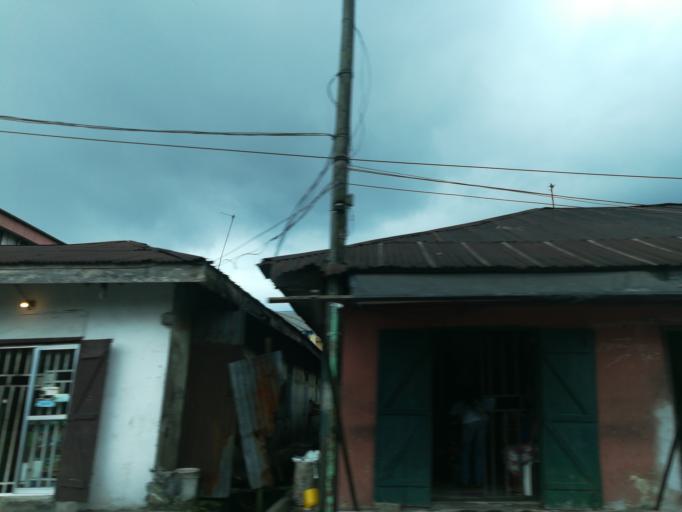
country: NG
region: Rivers
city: Port Harcourt
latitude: 4.7964
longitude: 6.9895
